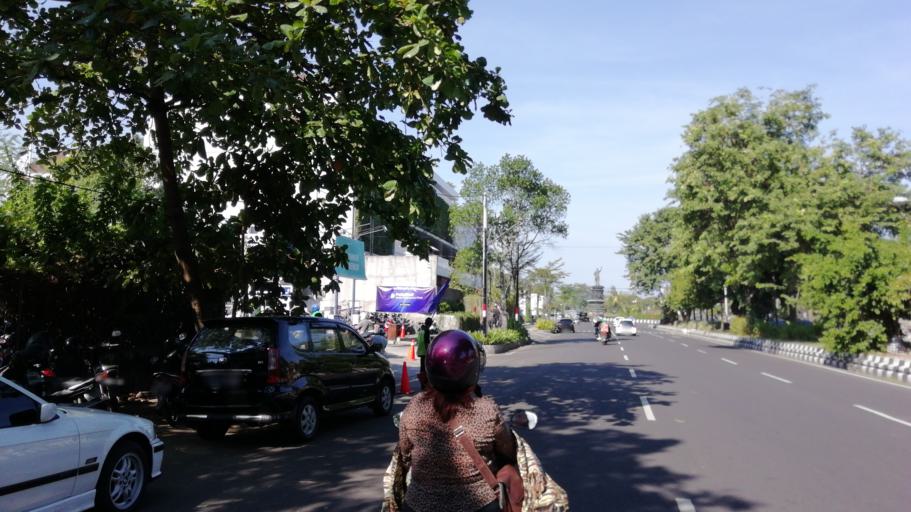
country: ID
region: Bali
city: Banjar Batanpoh
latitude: -8.6734
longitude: 115.2433
